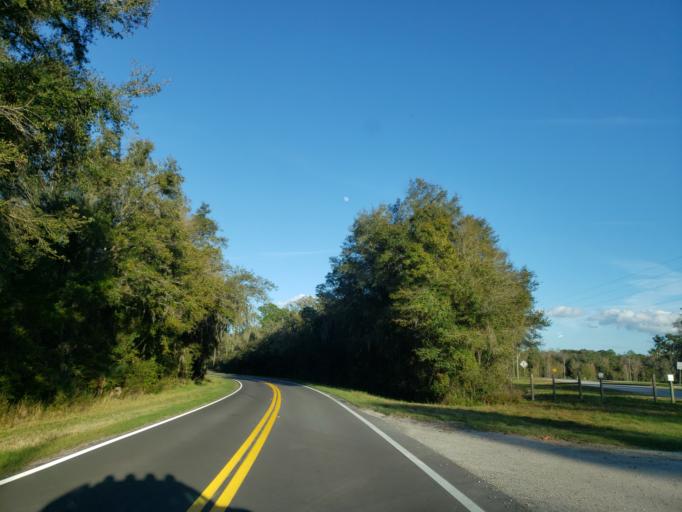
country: US
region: Florida
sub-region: Hillsborough County
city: Boyette
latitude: 27.8215
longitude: -82.2064
